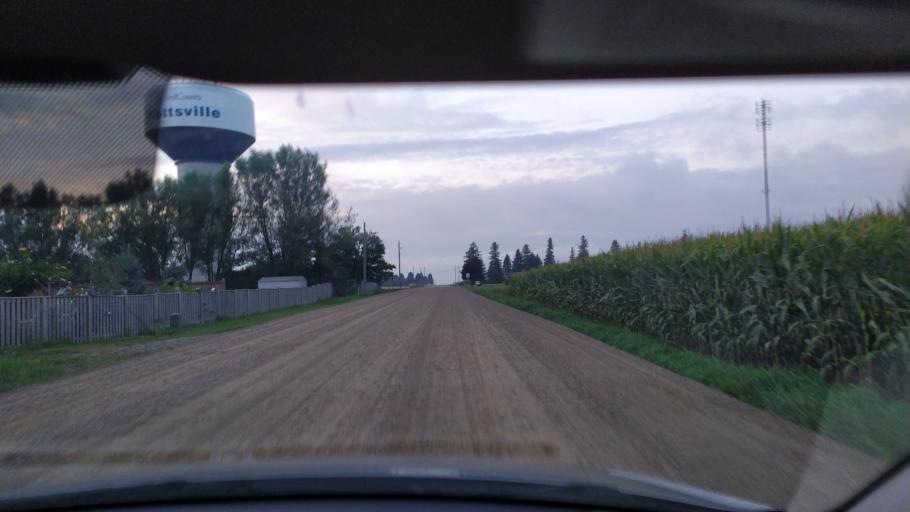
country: CA
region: Ontario
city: Kitchener
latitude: 43.3105
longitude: -80.6115
